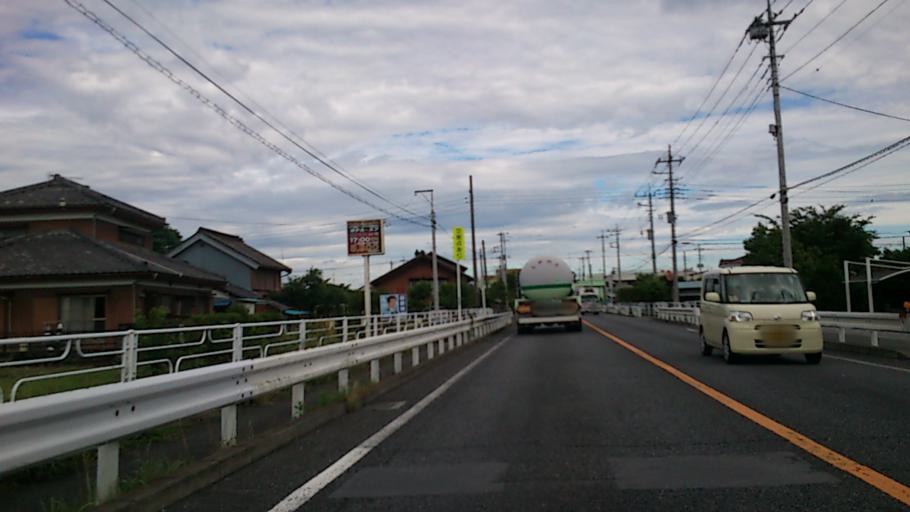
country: JP
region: Saitama
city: Honjo
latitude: 36.2577
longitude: 139.1538
